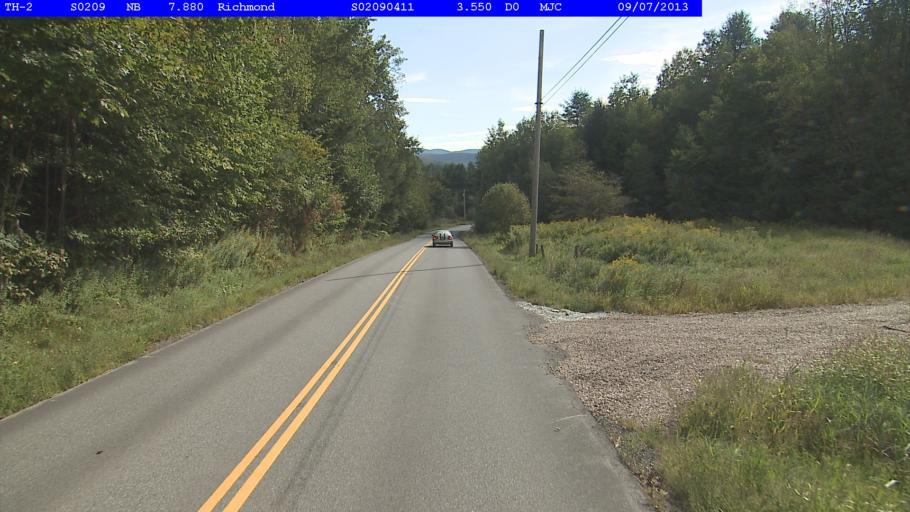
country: US
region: Vermont
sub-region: Chittenden County
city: Williston
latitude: 44.3993
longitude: -73.0199
